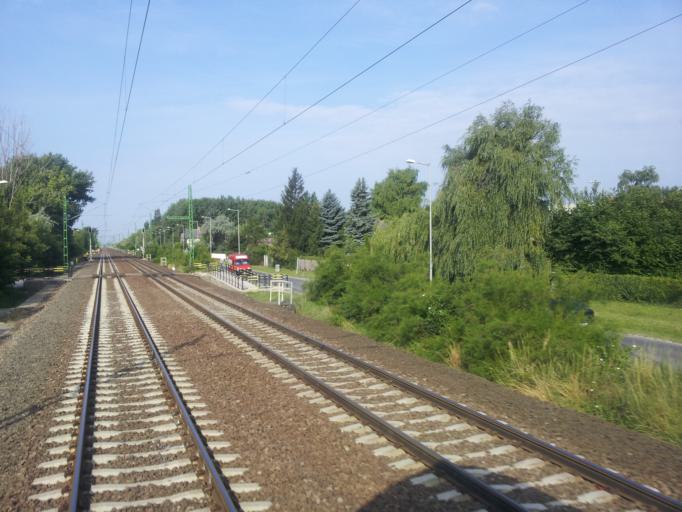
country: HU
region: Fejer
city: Gardony
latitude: 47.1940
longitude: 18.5961
